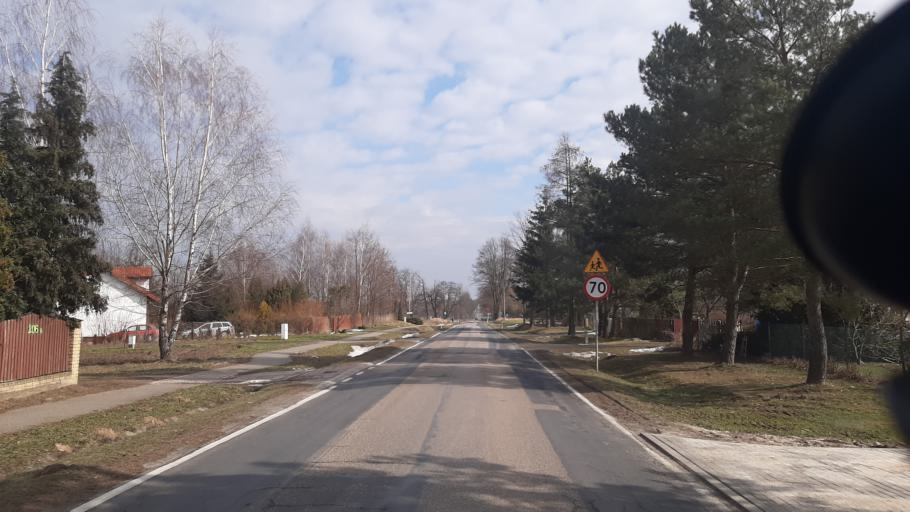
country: PL
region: Lublin Voivodeship
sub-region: Powiat lubelski
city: Niemce
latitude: 51.3606
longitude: 22.5497
